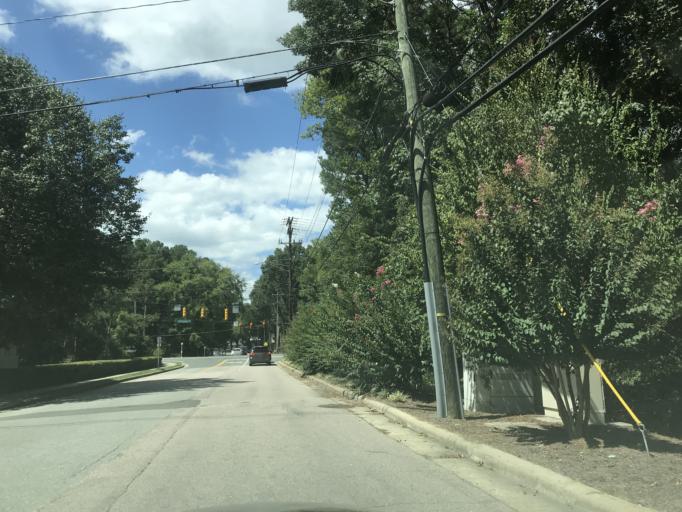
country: US
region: North Carolina
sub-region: Orange County
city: Chapel Hill
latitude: 35.9303
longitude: -79.0232
